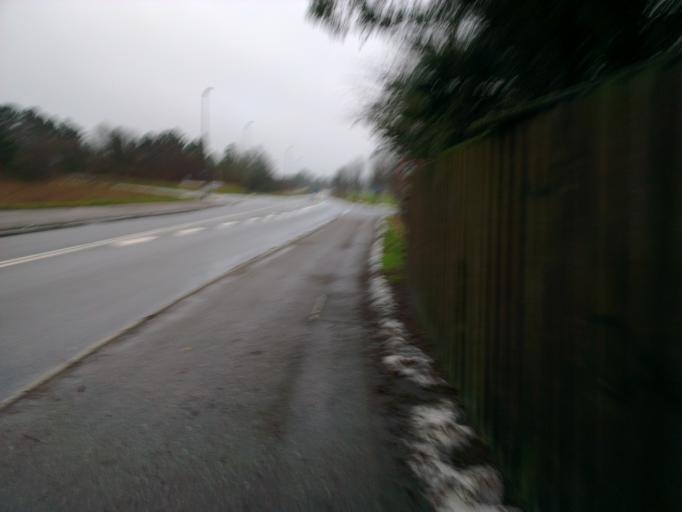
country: DK
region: Capital Region
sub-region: Frederikssund Kommune
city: Jaegerspris
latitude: 55.8334
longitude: 11.9882
